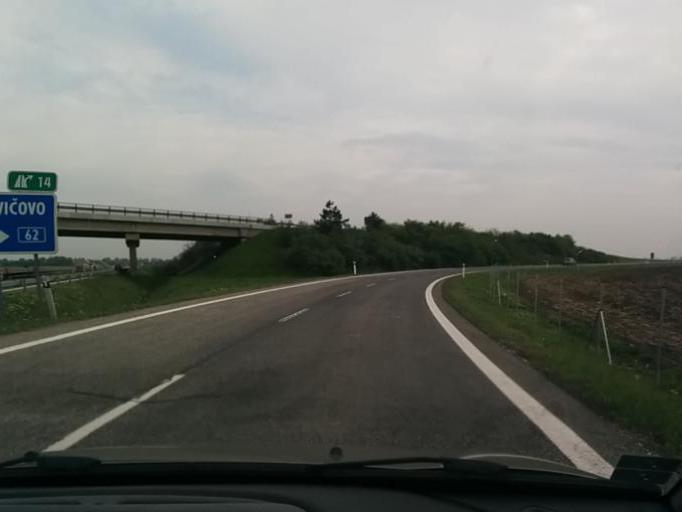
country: SK
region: Trnavsky
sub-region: Okres Galanta
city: Galanta
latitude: 48.2715
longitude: 17.7186
